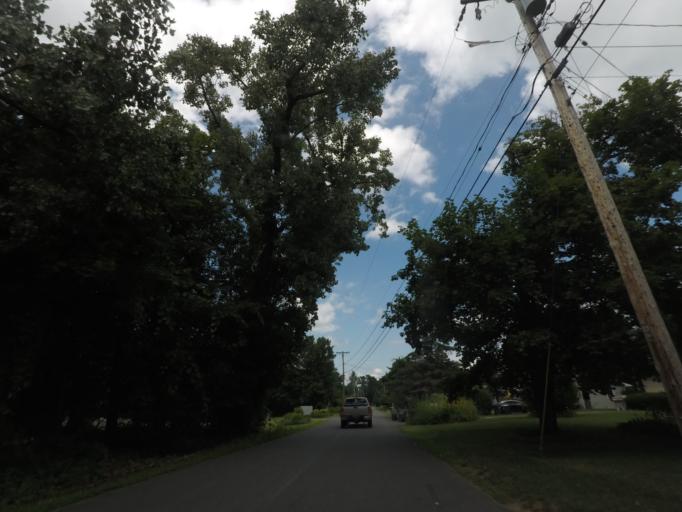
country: US
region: New York
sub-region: Rensselaer County
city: Castleton-on-Hudson
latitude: 42.5300
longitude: -73.6904
